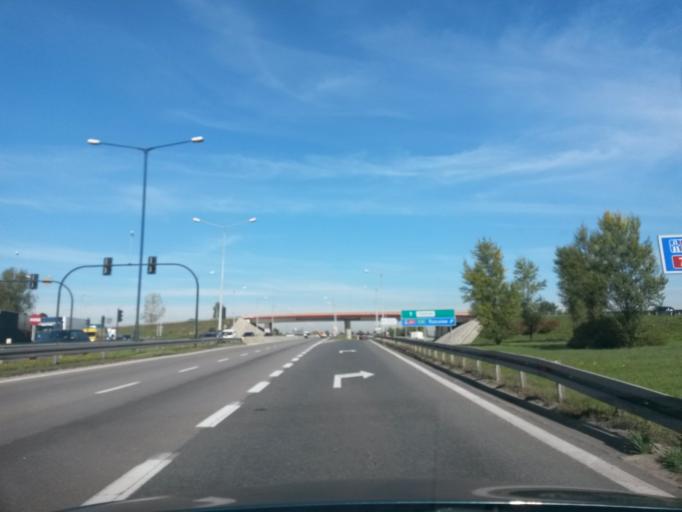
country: PL
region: Lesser Poland Voivodeship
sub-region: Powiat krakowski
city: Libertow
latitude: 49.9895
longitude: 19.9158
